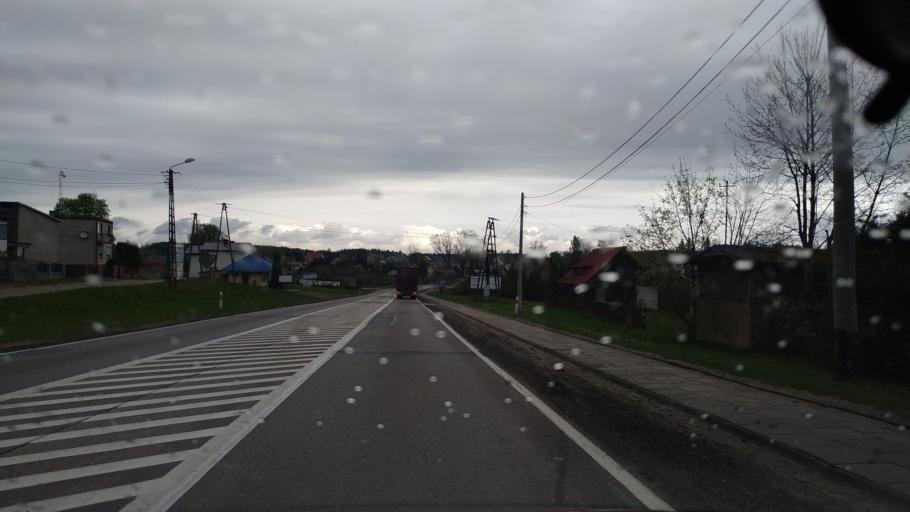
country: PL
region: Pomeranian Voivodeship
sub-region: Powiat starogardzki
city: Zblewo
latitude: 53.9187
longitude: 18.2787
